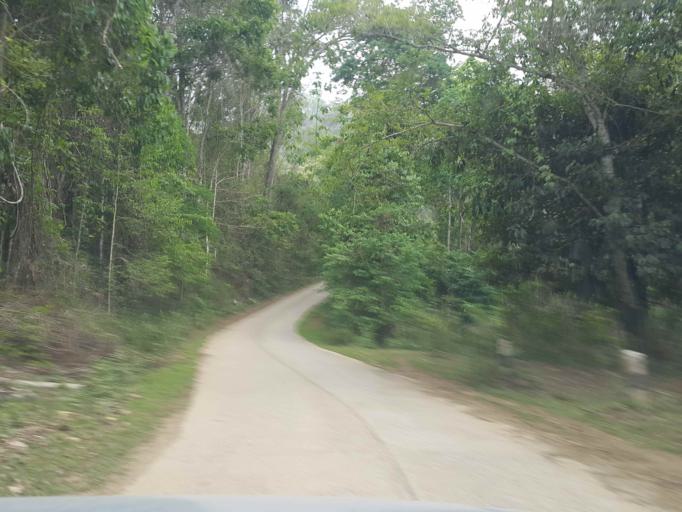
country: TH
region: Chiang Mai
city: Wiang Haeng
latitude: 19.3767
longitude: 98.7510
